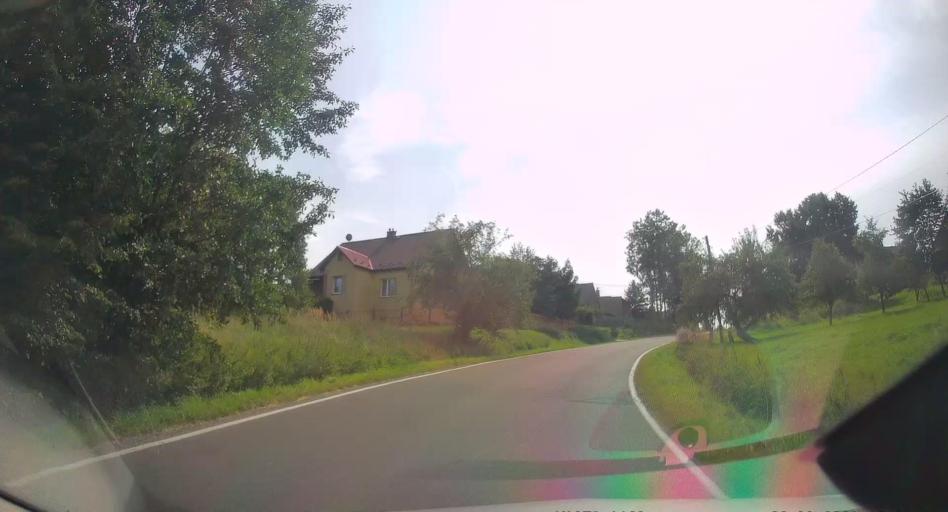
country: PL
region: Lesser Poland Voivodeship
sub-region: Powiat wielicki
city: Pawlikowice
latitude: 49.9496
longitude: 20.0423
